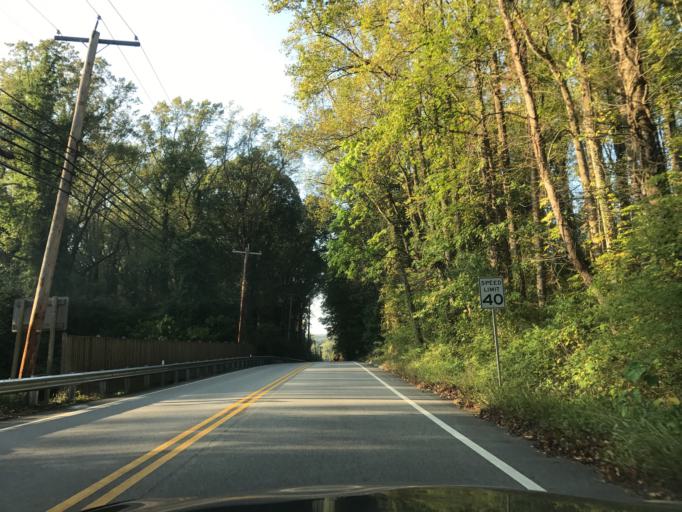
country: US
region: Maryland
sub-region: Anne Arundel County
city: Crownsville
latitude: 39.0492
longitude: -76.6153
